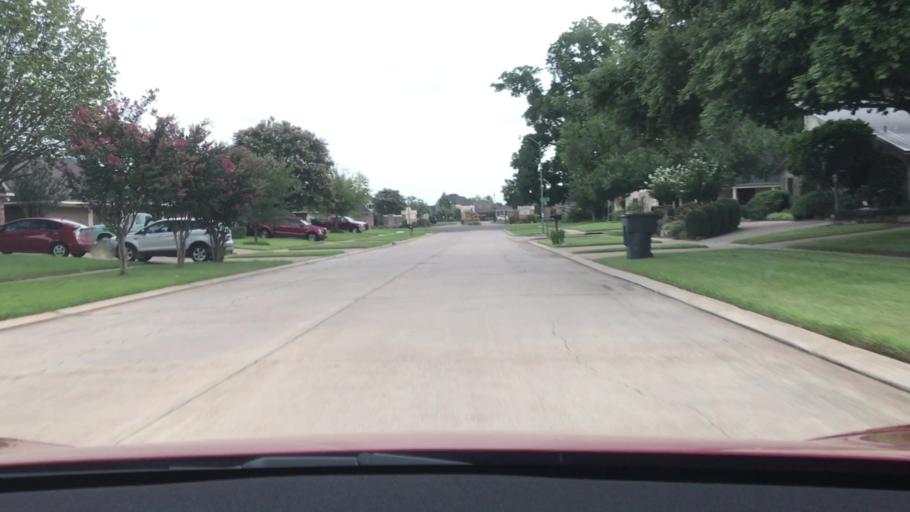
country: US
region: Louisiana
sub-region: Bossier Parish
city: Bossier City
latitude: 32.4543
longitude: -93.6706
